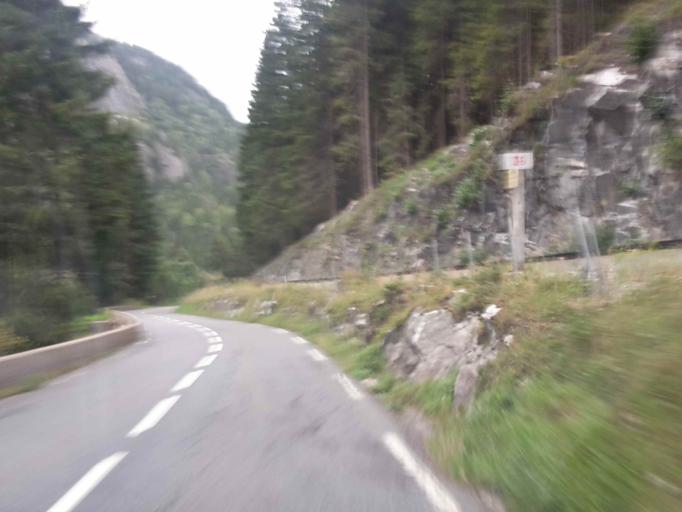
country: CH
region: Valais
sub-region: Saint-Maurice District
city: Salvan
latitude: 46.0474
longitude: 6.9424
